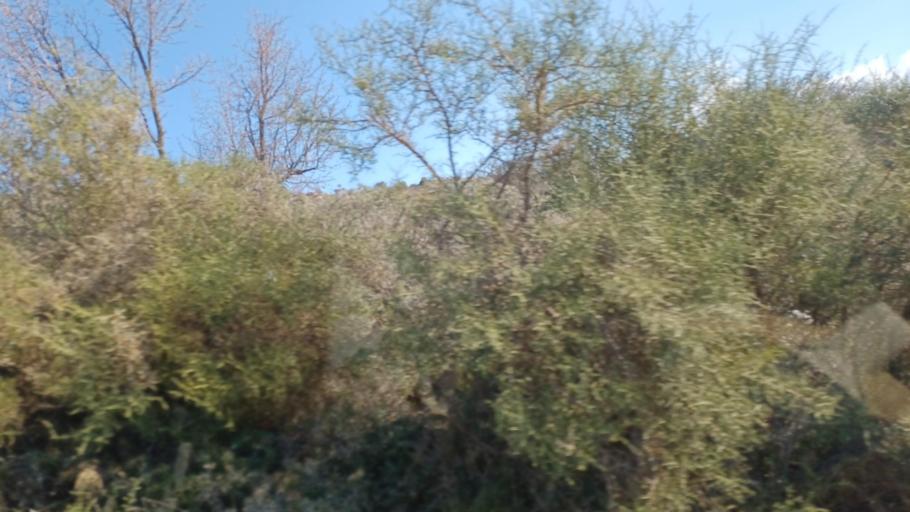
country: CY
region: Limassol
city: Pachna
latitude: 34.8216
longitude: 32.6887
